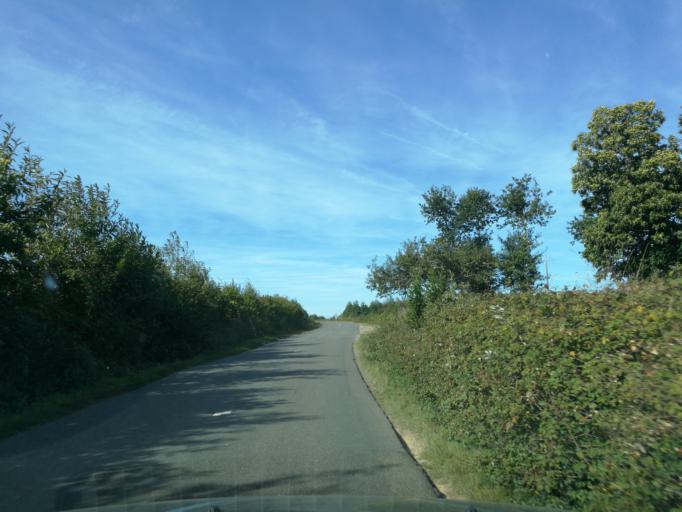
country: FR
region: Brittany
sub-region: Departement d'Ille-et-Vilaine
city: Breteil
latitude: 48.1666
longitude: -1.8961
